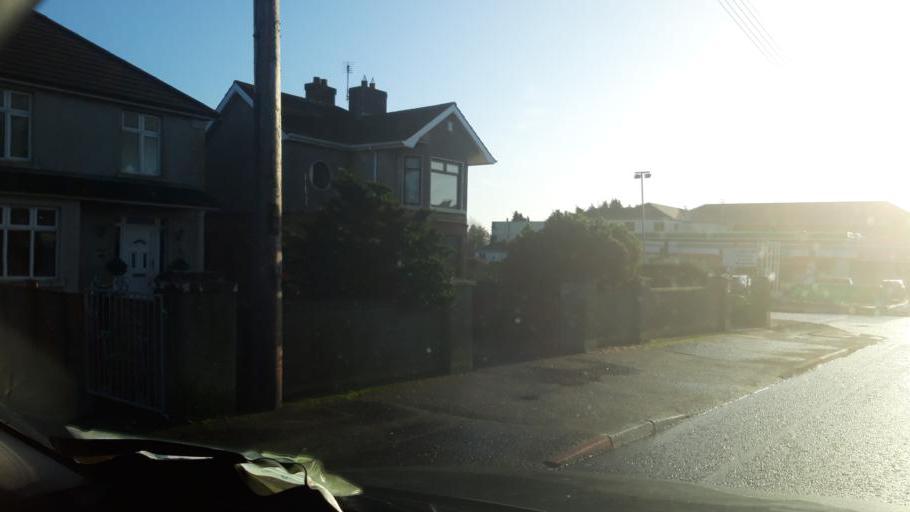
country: GB
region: Northern Ireland
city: Garvagh
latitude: 54.9859
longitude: -6.6863
